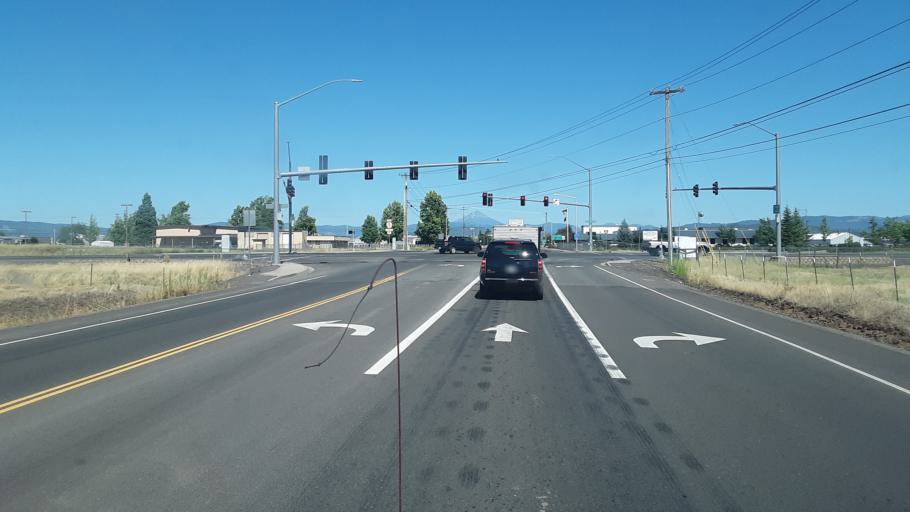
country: US
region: Oregon
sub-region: Jackson County
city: White City
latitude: 42.4274
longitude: -122.8869
